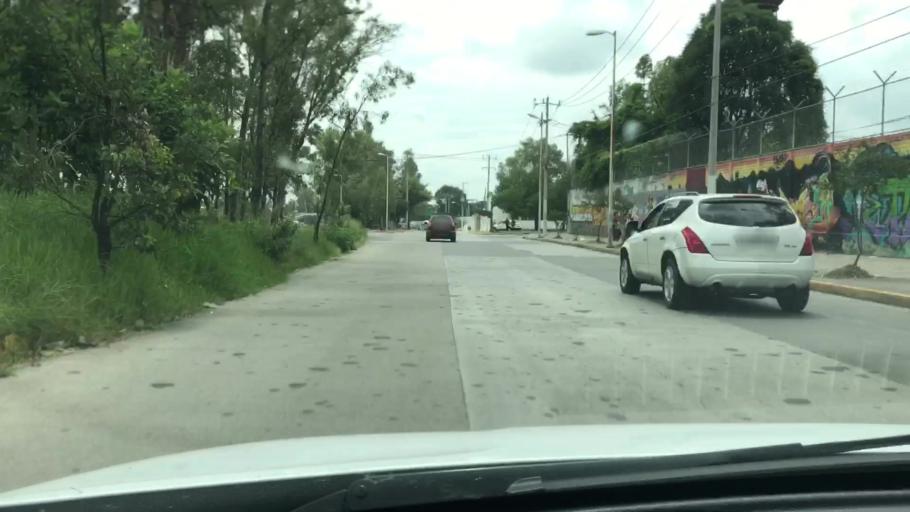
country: MX
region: Jalisco
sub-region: Tlajomulco de Zuniga
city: Palomar
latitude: 20.6423
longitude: -103.4413
